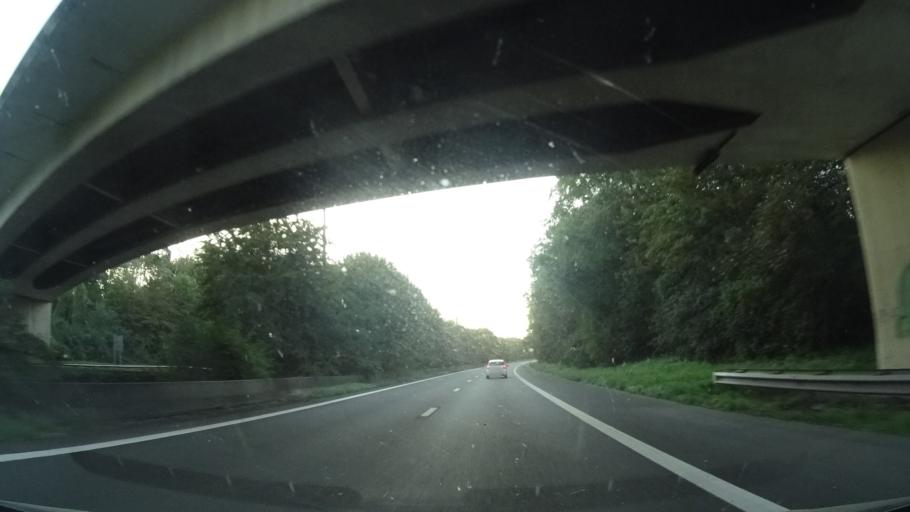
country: BE
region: Wallonia
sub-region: Province du Hainaut
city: Bernissart
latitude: 50.5098
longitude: 3.6674
